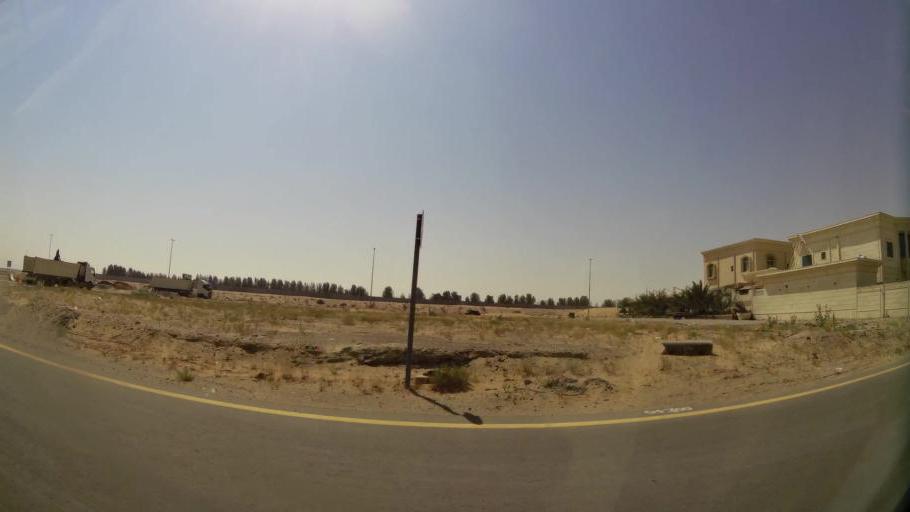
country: AE
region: Ajman
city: Ajman
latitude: 25.4117
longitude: 55.5546
